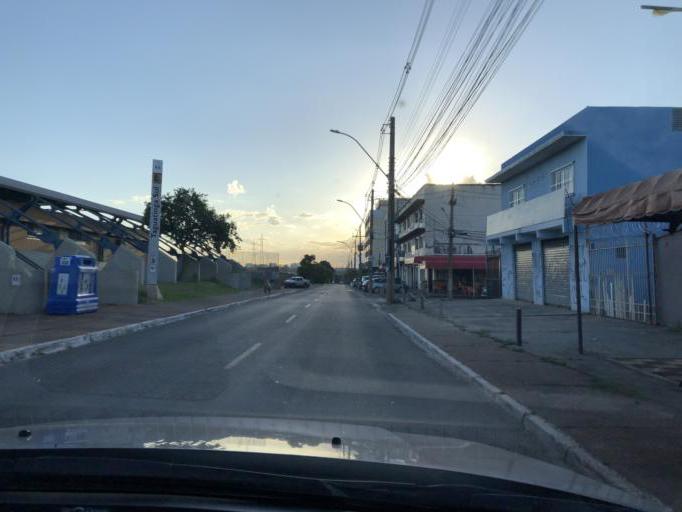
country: BR
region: Federal District
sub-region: Brasilia
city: Brasilia
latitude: -15.8513
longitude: -48.0417
